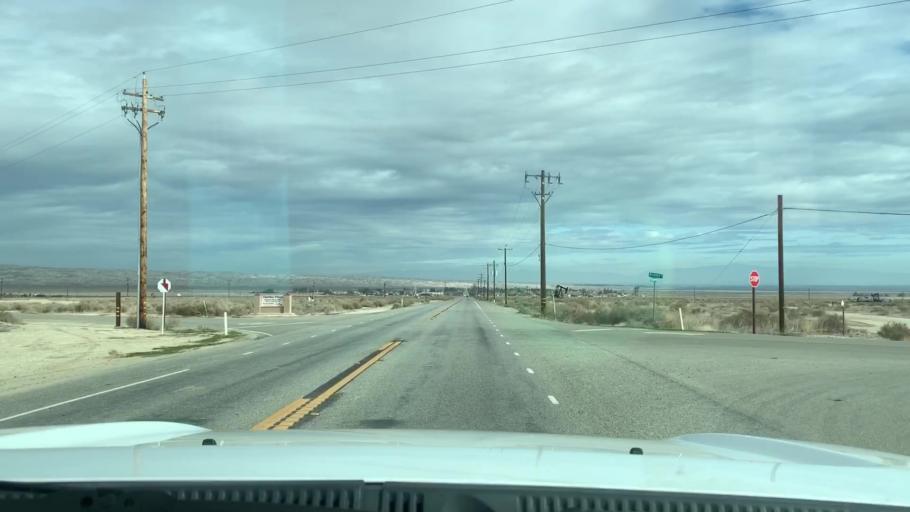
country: US
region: California
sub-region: Kern County
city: Ford City
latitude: 35.1935
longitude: -119.4292
